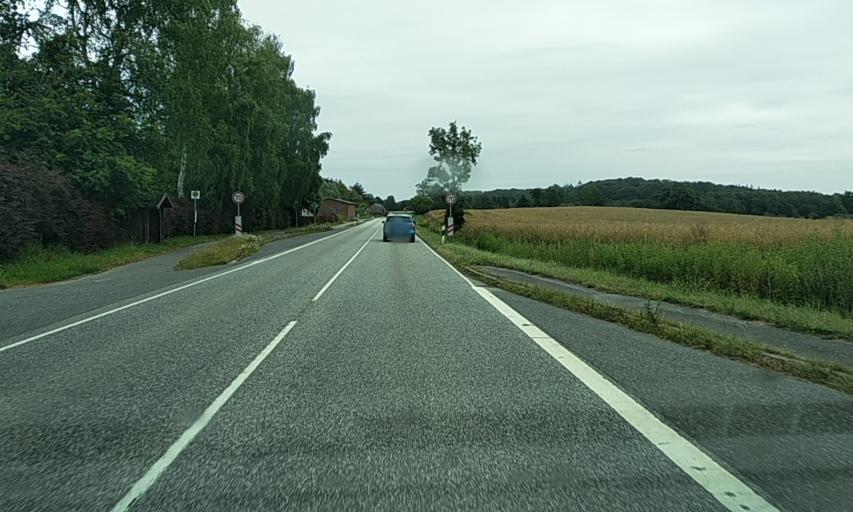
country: DE
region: Schleswig-Holstein
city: Rabenkirchen-Fauluck
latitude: 54.6448
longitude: 9.8766
